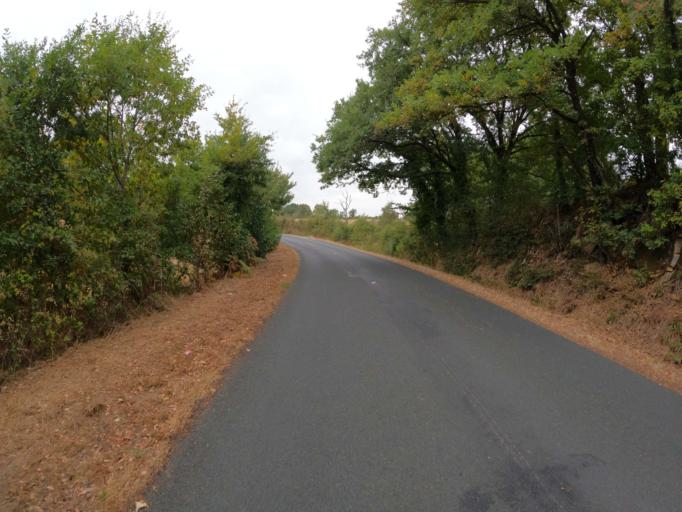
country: FR
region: Pays de la Loire
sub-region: Departement de la Vendee
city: Tiffauges
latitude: 46.9931
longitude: -1.1083
